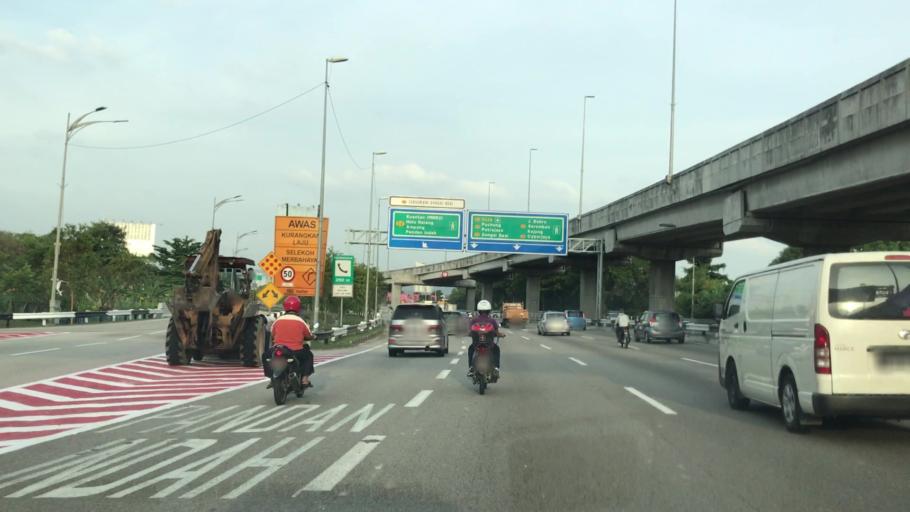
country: MY
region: Kuala Lumpur
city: Kuala Lumpur
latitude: 3.1229
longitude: 101.7050
